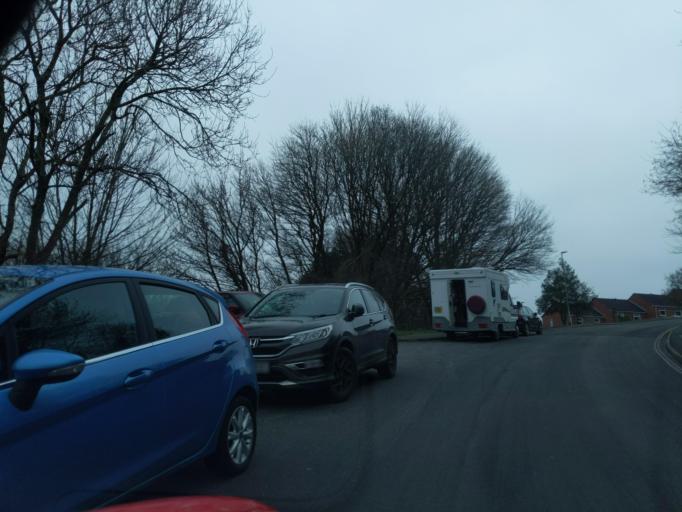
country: GB
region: England
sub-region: Plymouth
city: Plymstock
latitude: 50.3933
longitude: -4.0991
